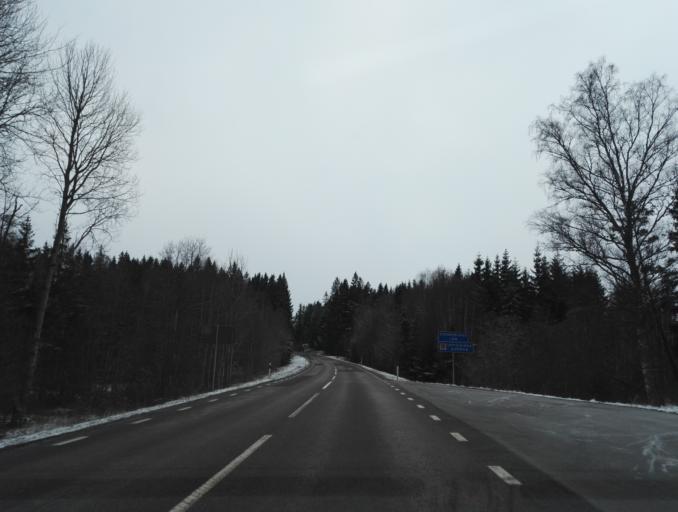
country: SE
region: Kalmar
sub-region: Hultsfreds Kommun
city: Virserum
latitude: 57.2023
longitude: 15.5149
